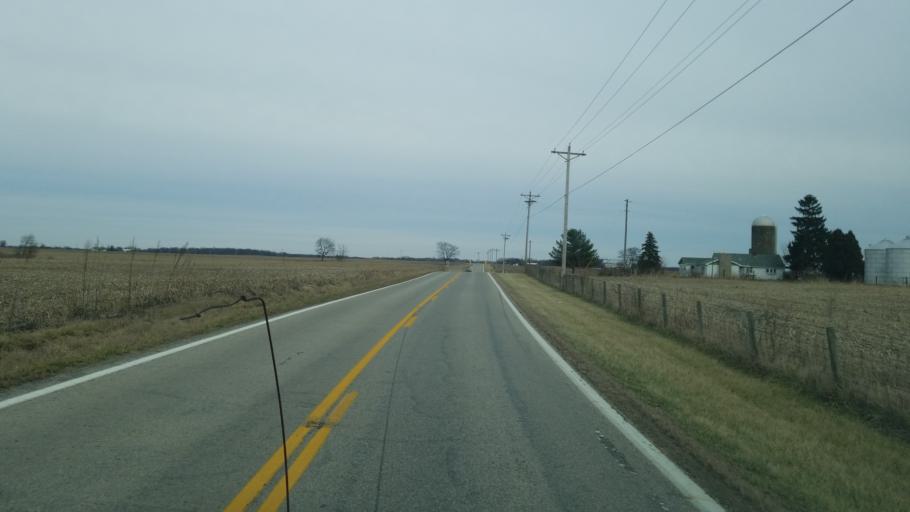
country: US
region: Ohio
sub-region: Pickaway County
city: Williamsport
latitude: 39.5237
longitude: -83.1317
